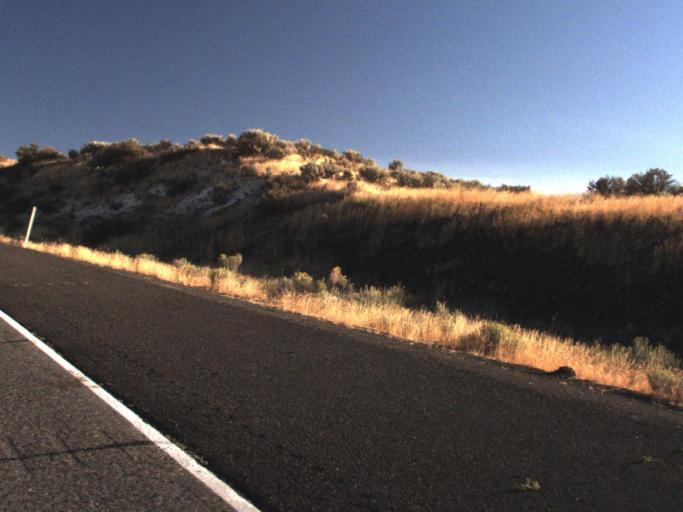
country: US
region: Washington
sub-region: Kittitas County
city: Kittitas
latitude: 46.8119
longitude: -120.3523
